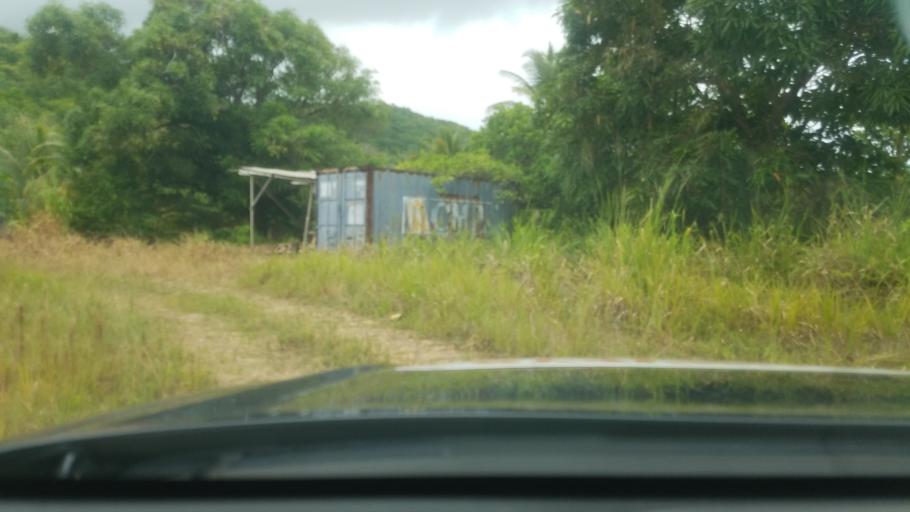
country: LC
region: Praslin
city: Praslin
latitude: 13.8657
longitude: -60.9016
